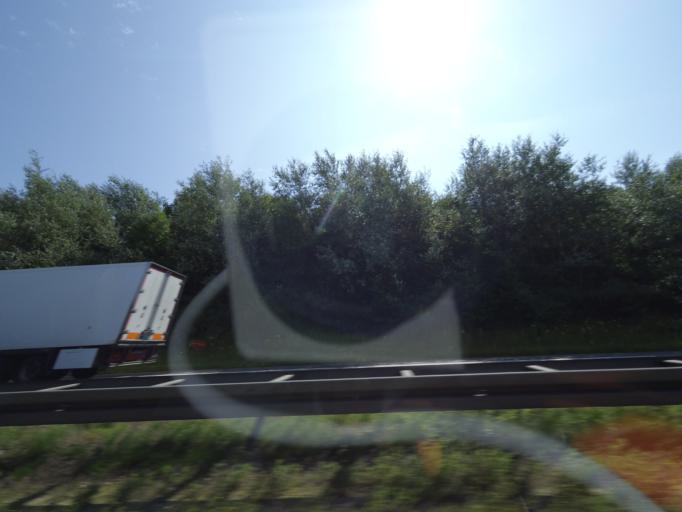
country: DK
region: Central Jutland
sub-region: Horsens Kommune
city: Horsens
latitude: 55.9511
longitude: 9.8312
